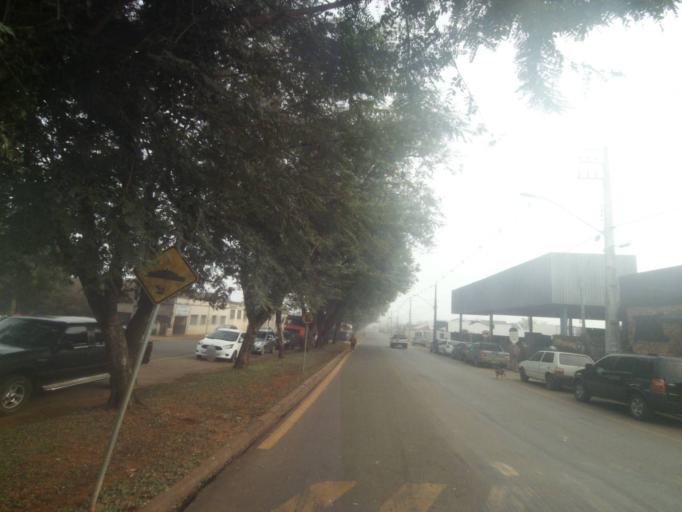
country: BR
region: Parana
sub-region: Tibagi
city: Tibagi
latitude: -24.5182
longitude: -50.4131
